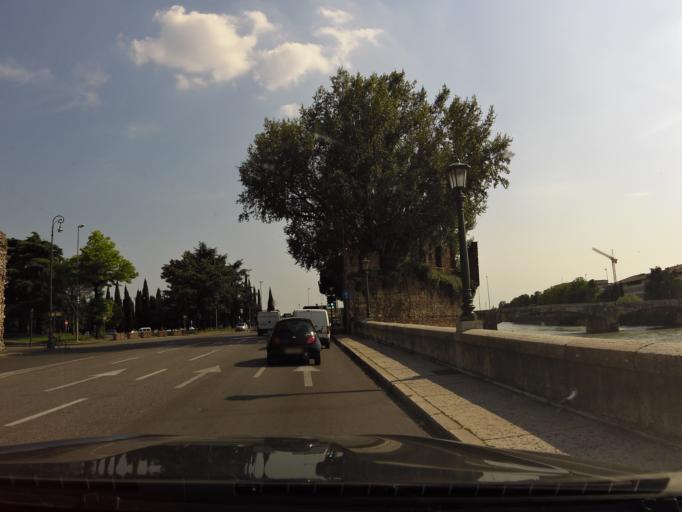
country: IT
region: Veneto
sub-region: Provincia di Verona
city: Verona
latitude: 45.4363
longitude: 11.0015
